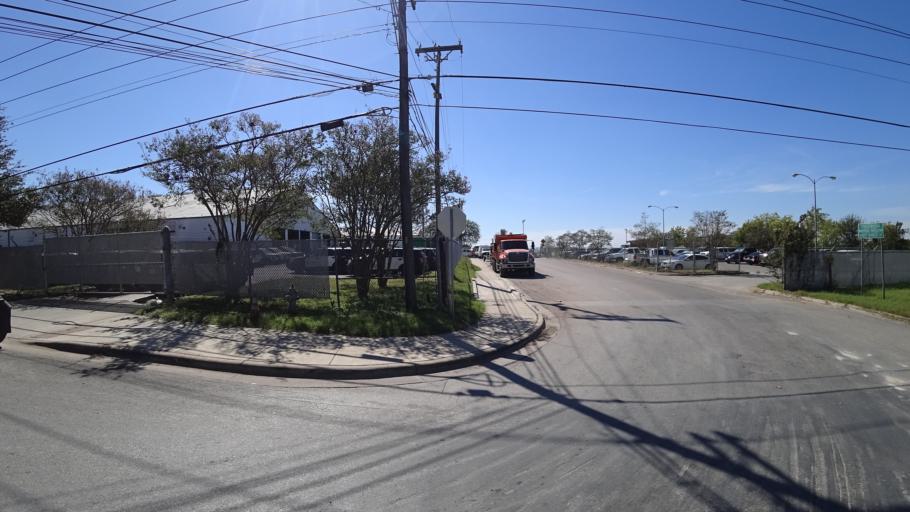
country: US
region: Texas
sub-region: Travis County
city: Austin
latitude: 30.2680
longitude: -97.6732
